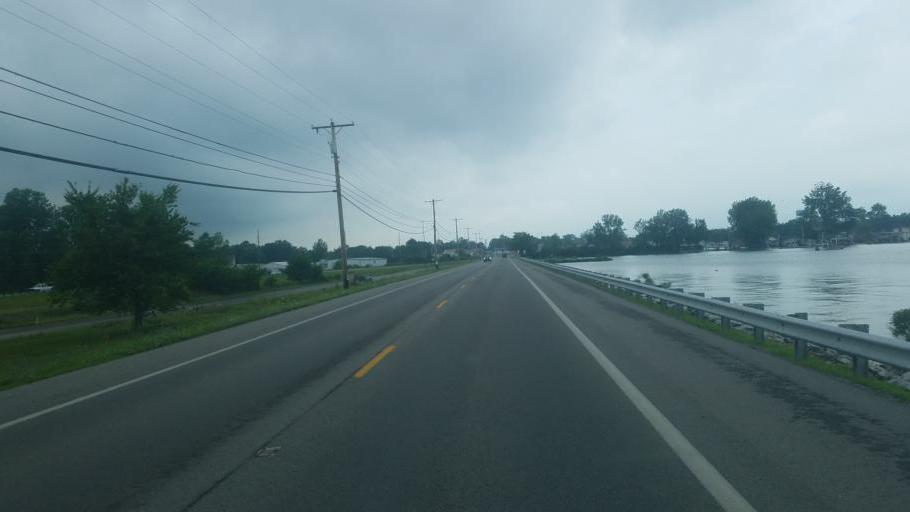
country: US
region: Ohio
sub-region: Logan County
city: Russells Point
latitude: 40.4673
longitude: -83.8822
